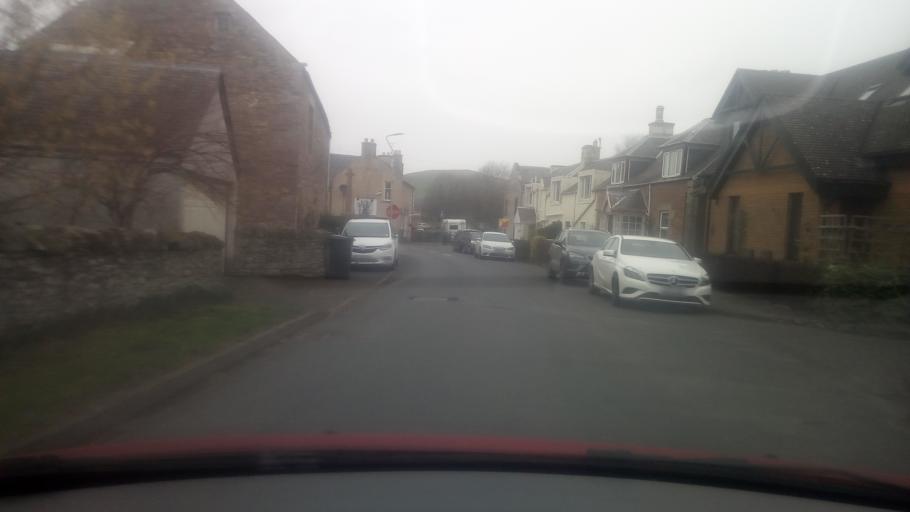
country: GB
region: Scotland
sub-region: The Scottish Borders
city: Hawick
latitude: 55.4565
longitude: -2.6845
